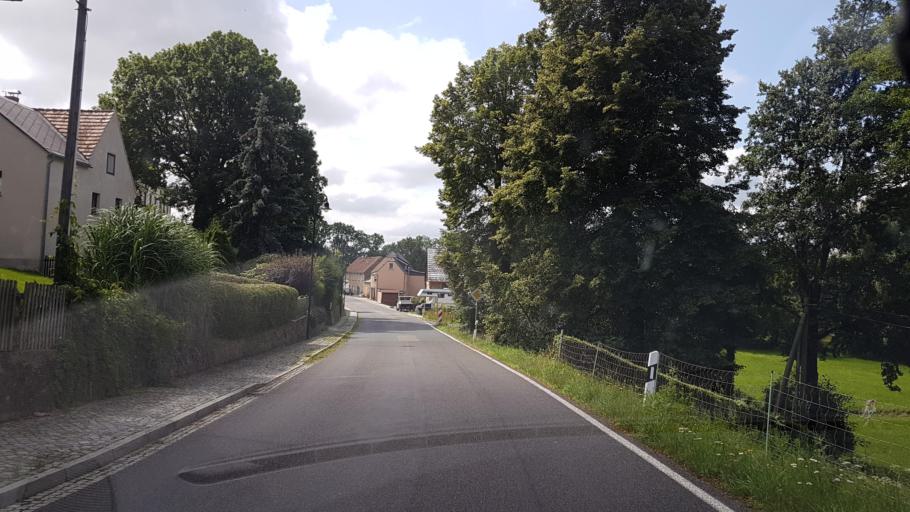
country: DE
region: Saxony
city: Wachau
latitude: 51.1662
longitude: 13.9066
